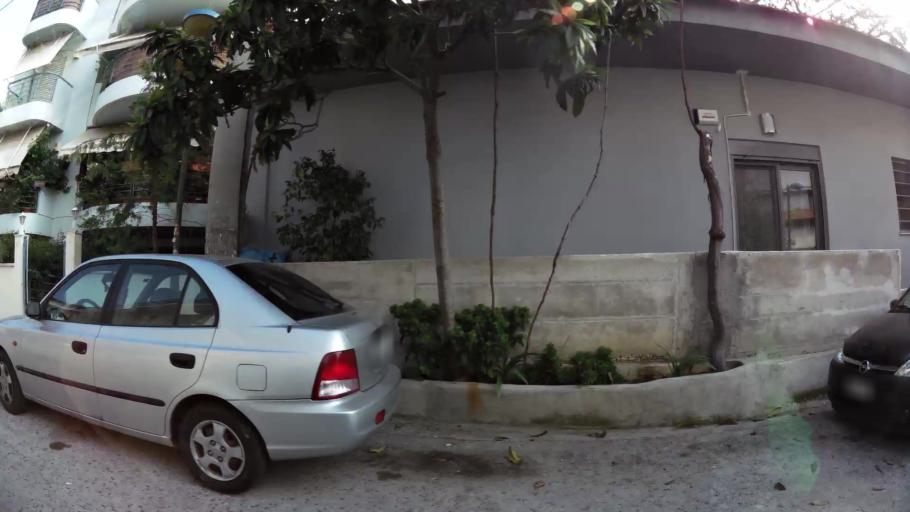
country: GR
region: Attica
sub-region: Nomarchia Athinas
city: Irakleio
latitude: 38.0561
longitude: 23.7474
